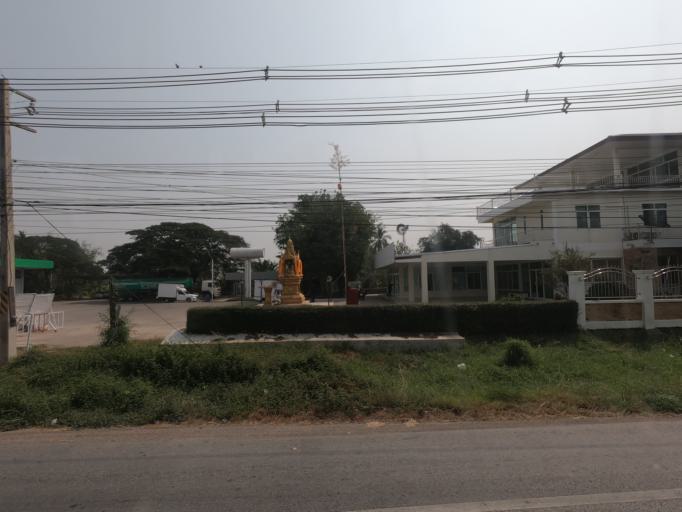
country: TH
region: Nakhon Ratchasima
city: Phimai
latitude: 15.2568
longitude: 102.4149
